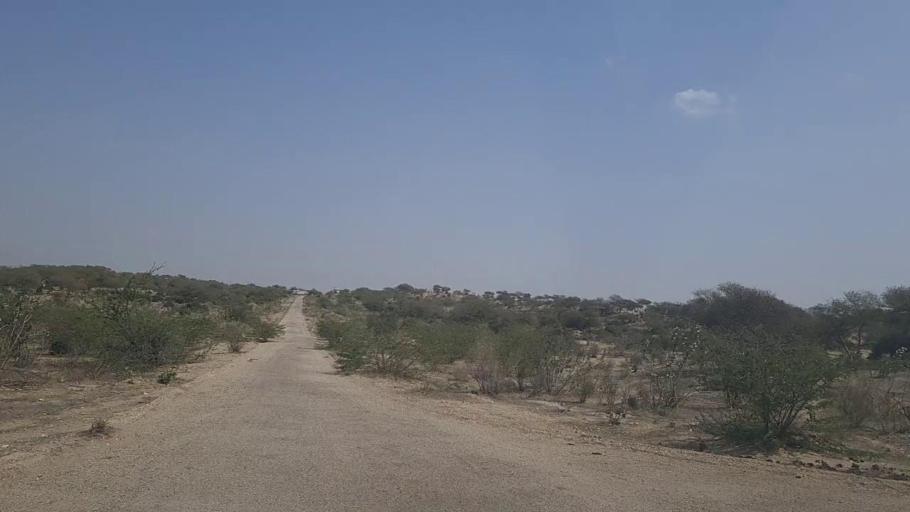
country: PK
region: Sindh
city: Naukot
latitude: 24.8179
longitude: 69.5006
